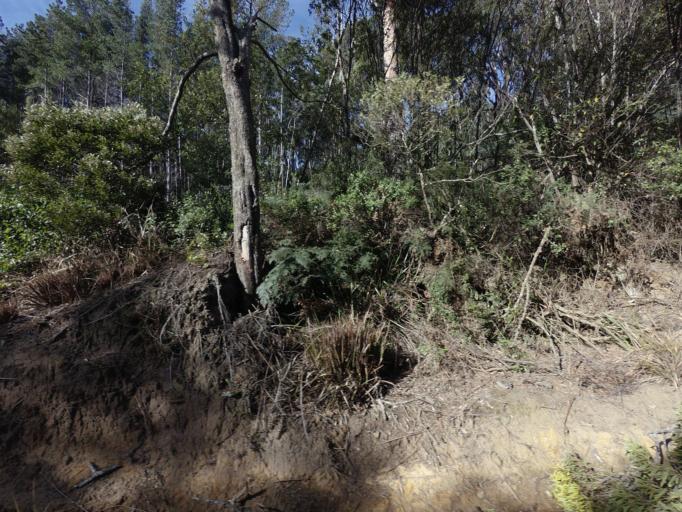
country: AU
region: Tasmania
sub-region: Clarence
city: Sandford
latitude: -43.1790
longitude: 147.7716
